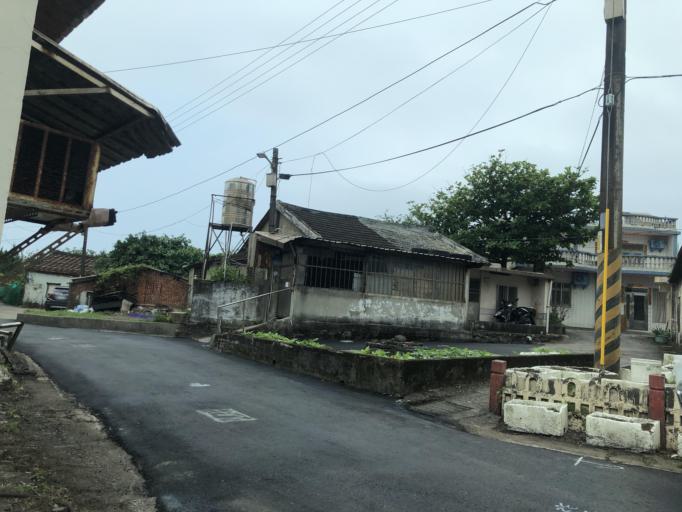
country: TW
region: Taiwan
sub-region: Keelung
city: Keelung
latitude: 25.2112
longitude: 121.6563
